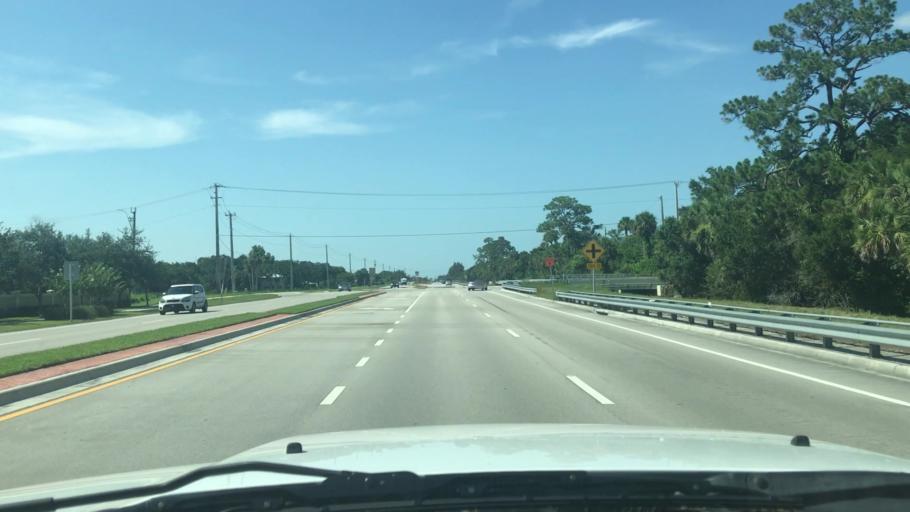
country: US
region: Florida
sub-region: Indian River County
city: West Vero Corridor
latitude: 27.6525
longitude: -80.4631
